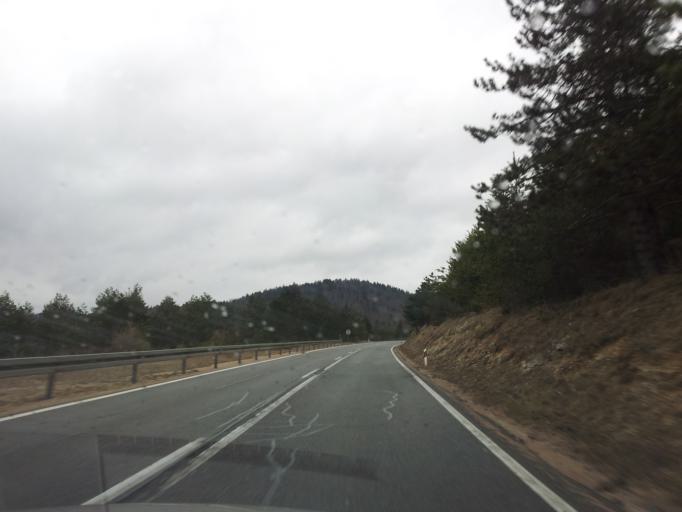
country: HR
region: Licko-Senjska
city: Jezerce
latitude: 44.7830
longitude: 15.6877
